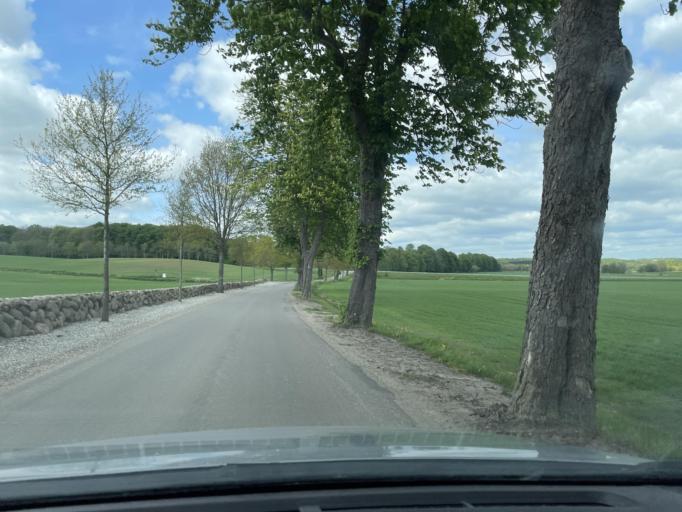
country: DK
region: Central Jutland
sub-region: Odder Kommune
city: Odder
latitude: 55.9130
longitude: 10.1004
